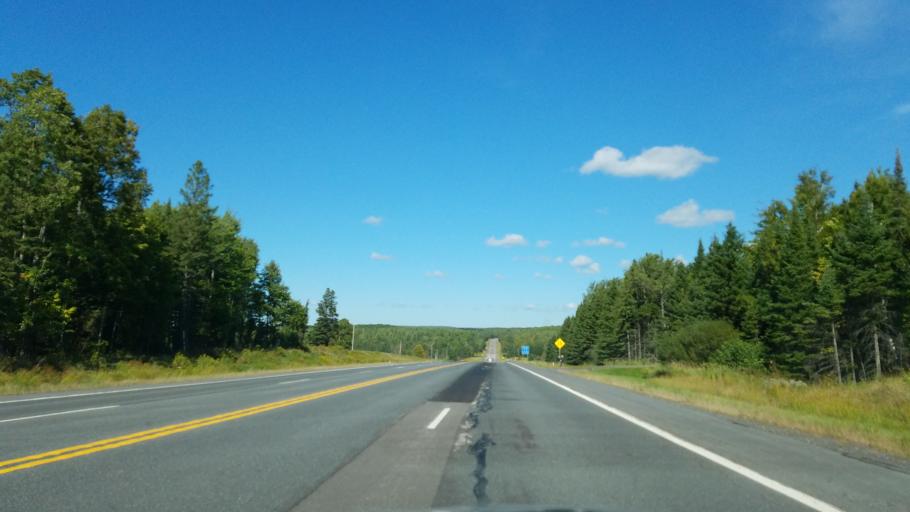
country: US
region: Michigan
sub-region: Baraga County
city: L'Anse
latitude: 46.5673
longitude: -88.5015
